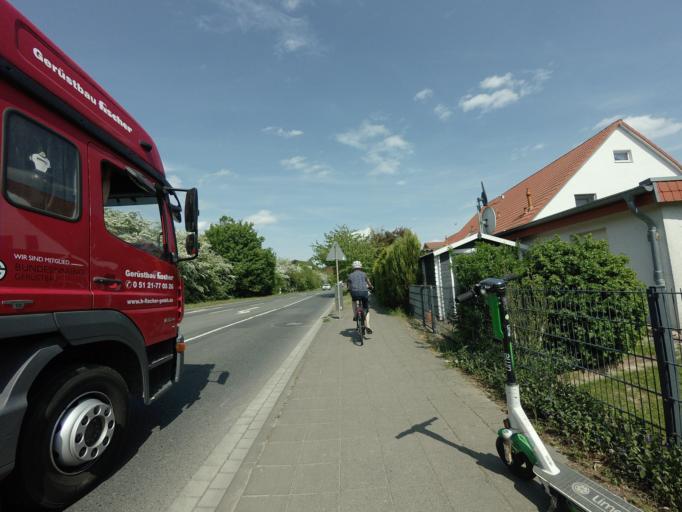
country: DE
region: Lower Saxony
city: Giesen
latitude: 52.1611
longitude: 9.9019
